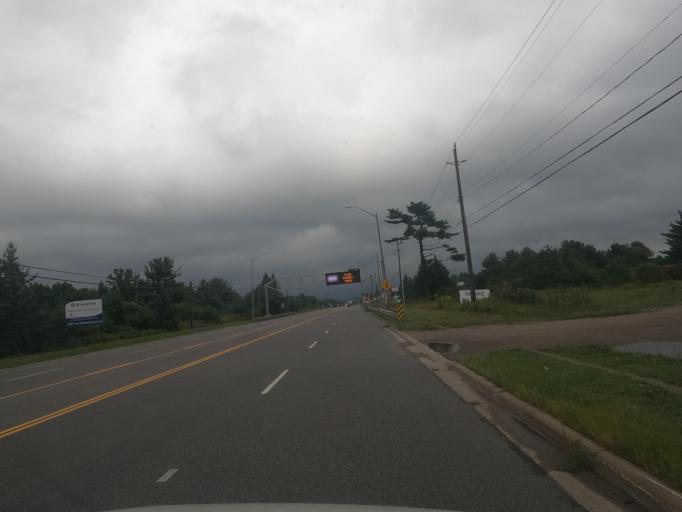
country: CA
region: Ontario
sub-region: Algoma
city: Sault Ste. Marie
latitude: 46.5375
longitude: -84.2378
